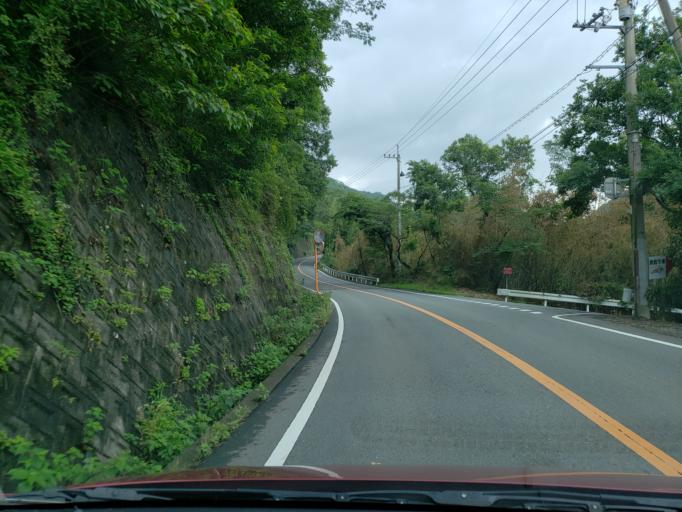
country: JP
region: Tokushima
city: Kamojimacho-jogejima
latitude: 34.1102
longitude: 134.2902
